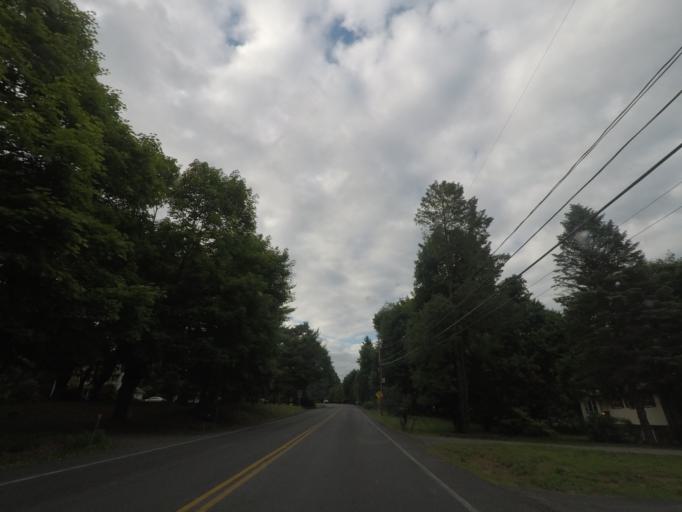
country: US
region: New York
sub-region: Orange County
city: Orange Lake
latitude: 41.5805
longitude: -74.1162
